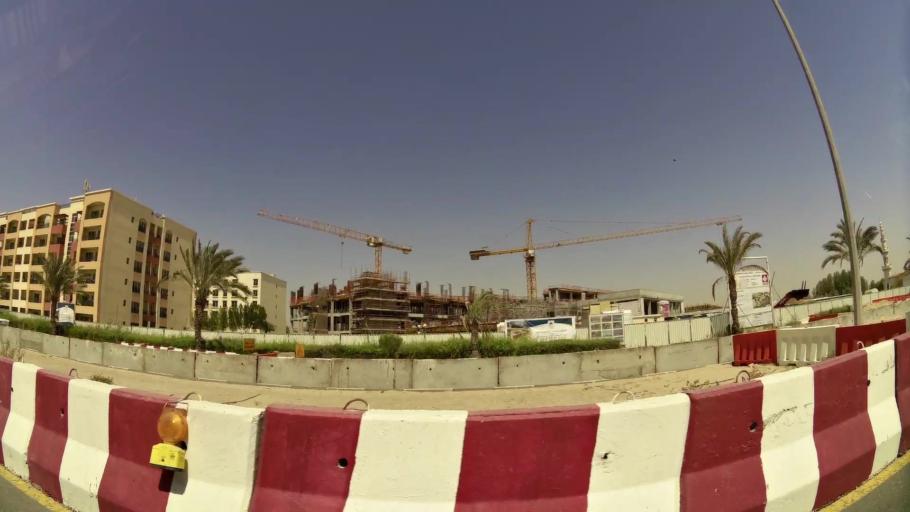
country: AE
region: Dubai
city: Dubai
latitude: 24.9984
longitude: 55.1543
